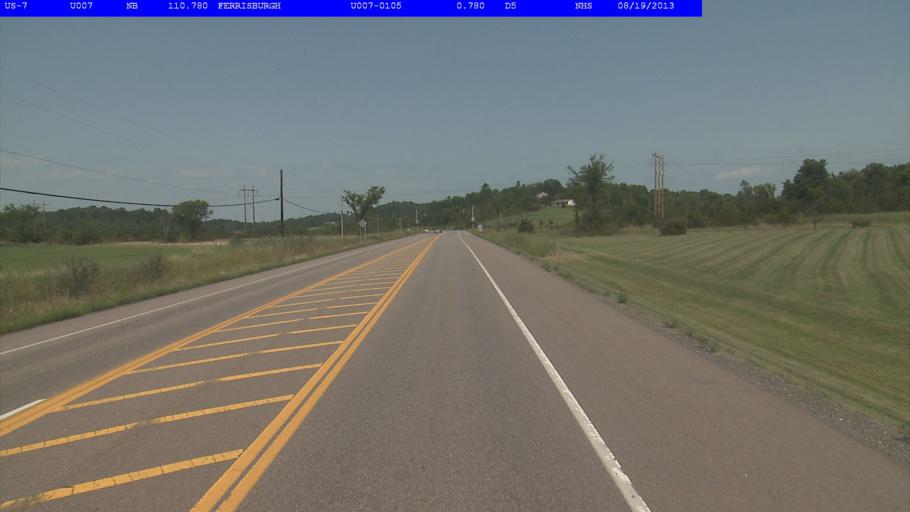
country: US
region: Vermont
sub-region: Addison County
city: Vergennes
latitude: 44.1729
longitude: -73.2394
